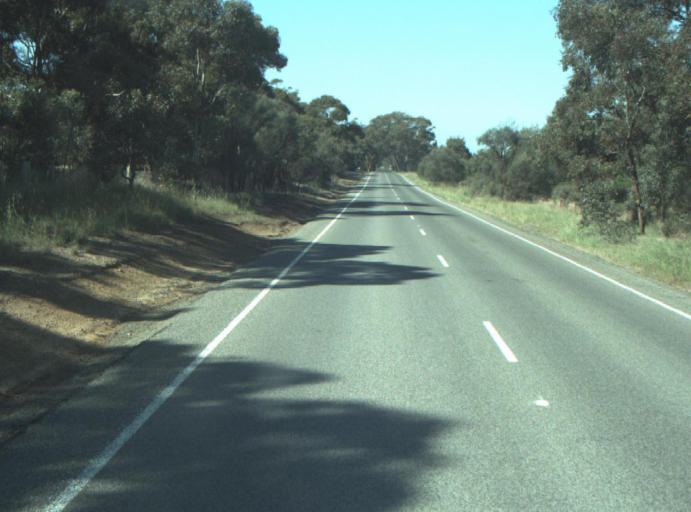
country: AU
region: Victoria
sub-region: Greater Geelong
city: Lara
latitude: -37.9138
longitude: 144.3978
